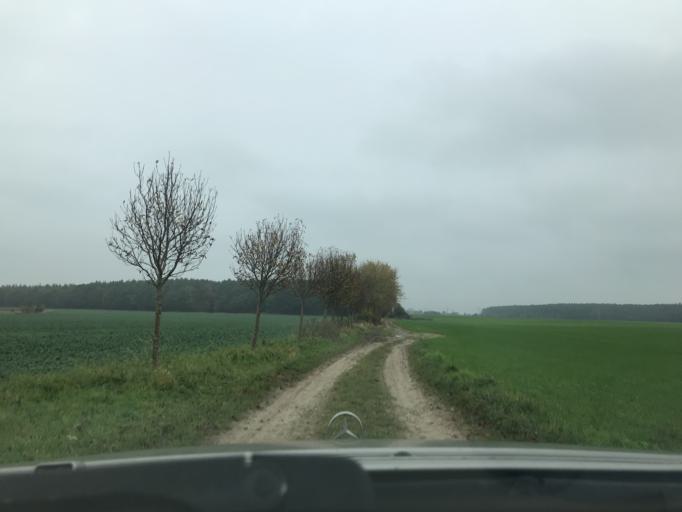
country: DE
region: Mecklenburg-Vorpommern
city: Kroslin
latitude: 54.1042
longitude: 13.7276
